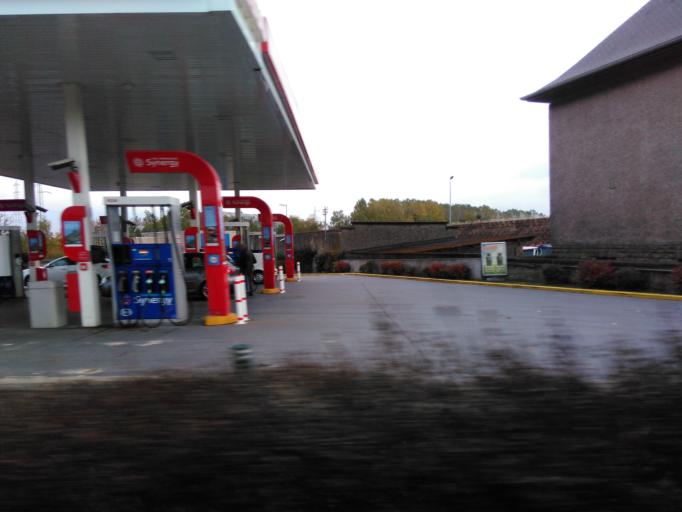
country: LU
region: Luxembourg
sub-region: Canton d'Esch-sur-Alzette
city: Esch-sur-Alzette
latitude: 49.5067
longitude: 5.9587
